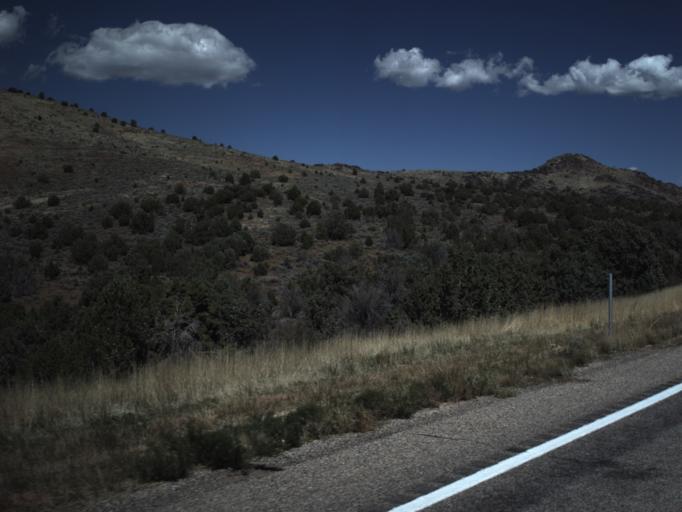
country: US
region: Utah
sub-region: Washington County
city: Ivins
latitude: 37.3603
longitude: -113.6734
